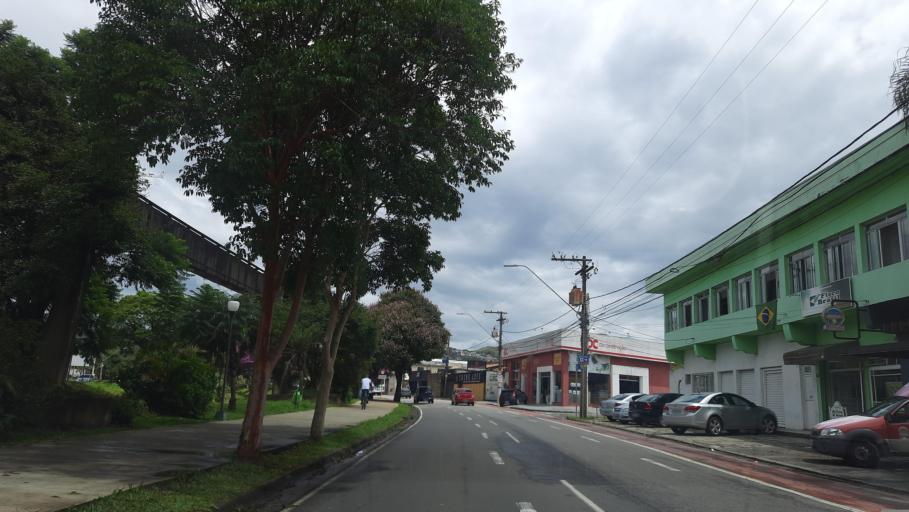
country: BR
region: Minas Gerais
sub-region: Pocos De Caldas
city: Pocos de Caldas
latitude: -21.7830
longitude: -46.5979
